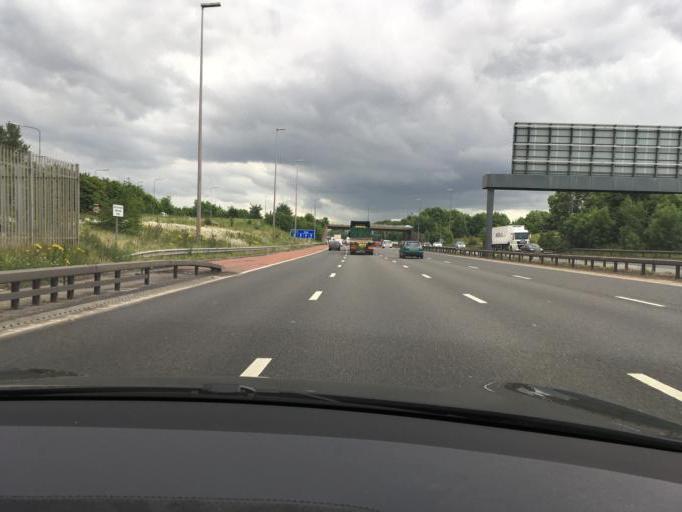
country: GB
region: England
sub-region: Manchester
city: Didsbury
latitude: 53.3990
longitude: -2.2257
